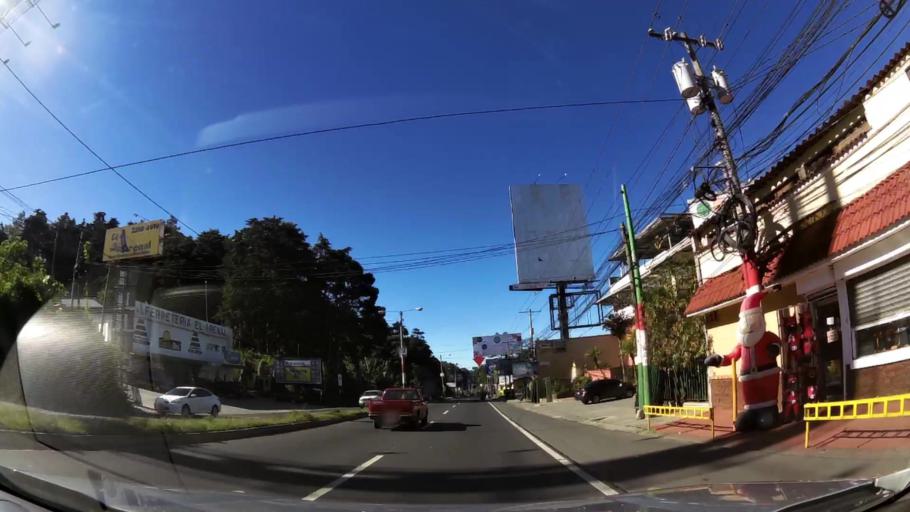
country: GT
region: Guatemala
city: San Jose Pinula
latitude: 14.5358
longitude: -90.4584
